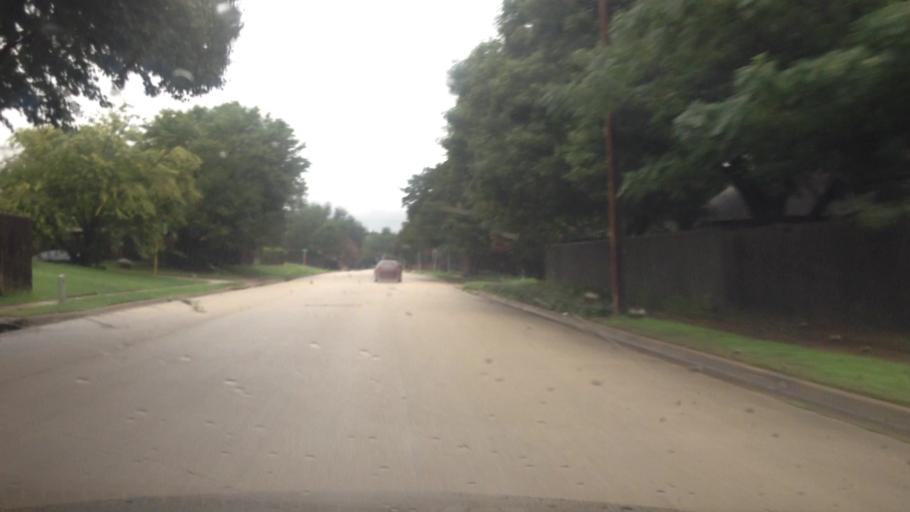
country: US
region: Texas
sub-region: Tarrant County
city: Colleyville
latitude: 32.8715
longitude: -97.1700
